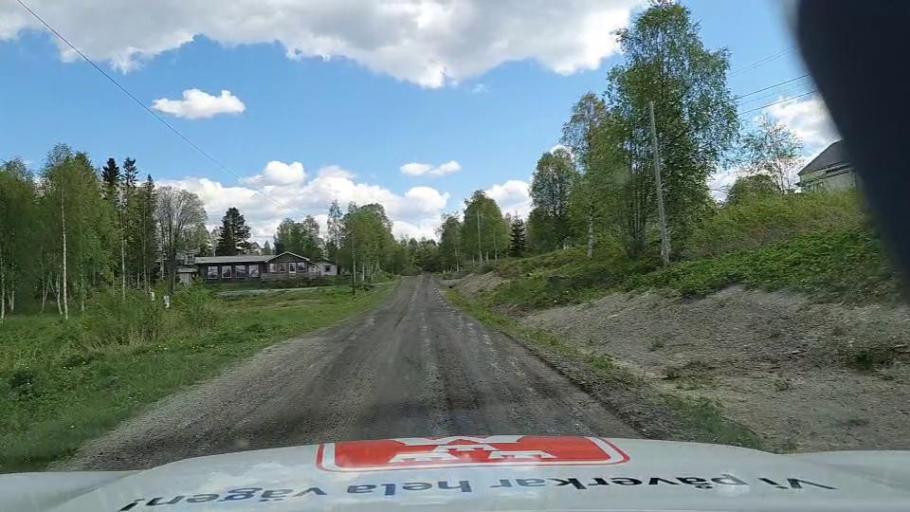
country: SE
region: Jaemtland
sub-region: Krokoms Kommun
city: Valla
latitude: 63.9623
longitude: 14.0516
